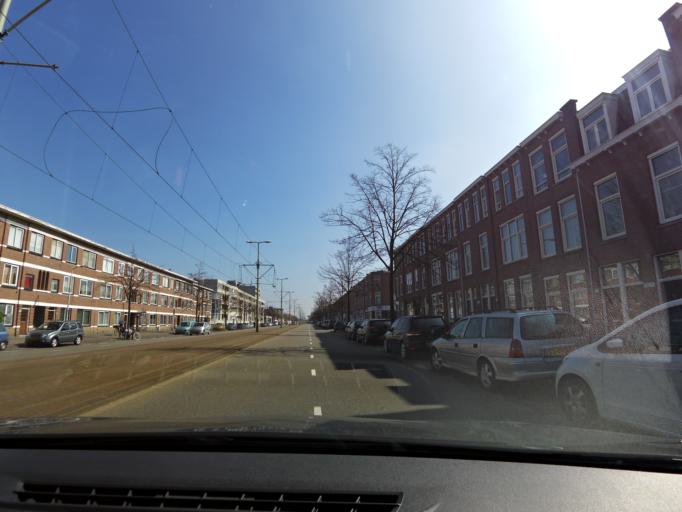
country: NL
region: South Holland
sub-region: Gemeente Rijswijk
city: Rijswijk
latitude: 52.0643
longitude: 4.3305
